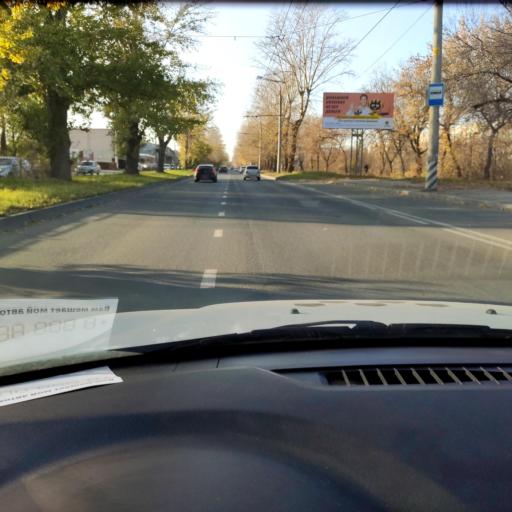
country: RU
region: Samara
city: Tol'yatti
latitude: 53.5156
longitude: 49.4392
